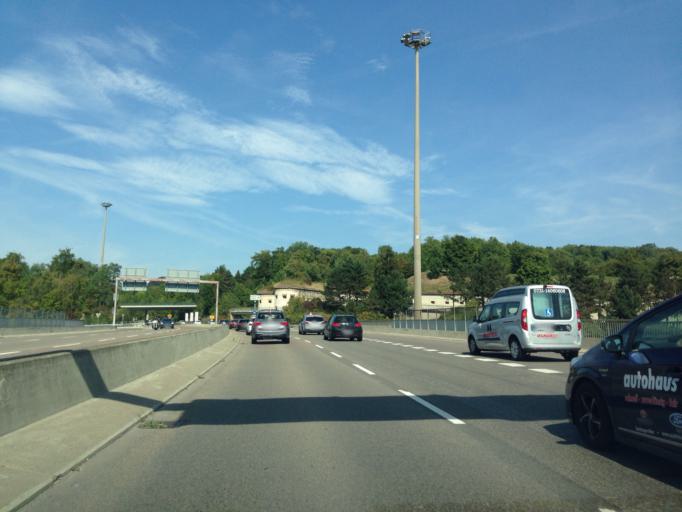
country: DE
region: Baden-Wuerttemberg
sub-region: Tuebingen Region
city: Ulm
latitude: 48.4049
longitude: 9.9789
